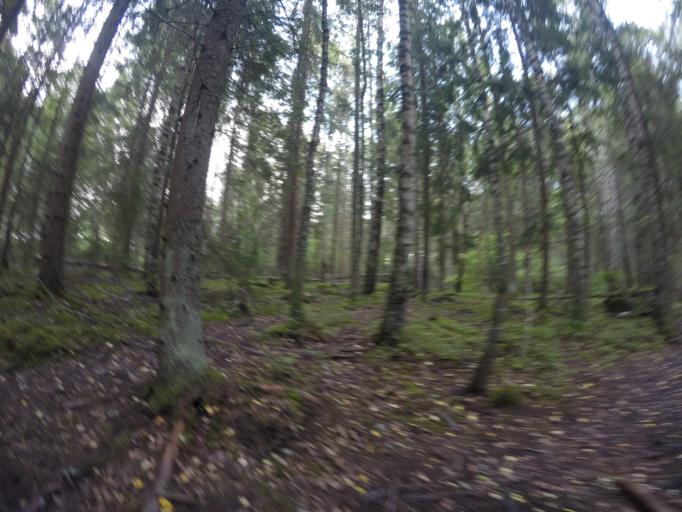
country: SE
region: Vaestmanland
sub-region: Vasteras
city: Vasteras
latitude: 59.6412
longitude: 16.5225
